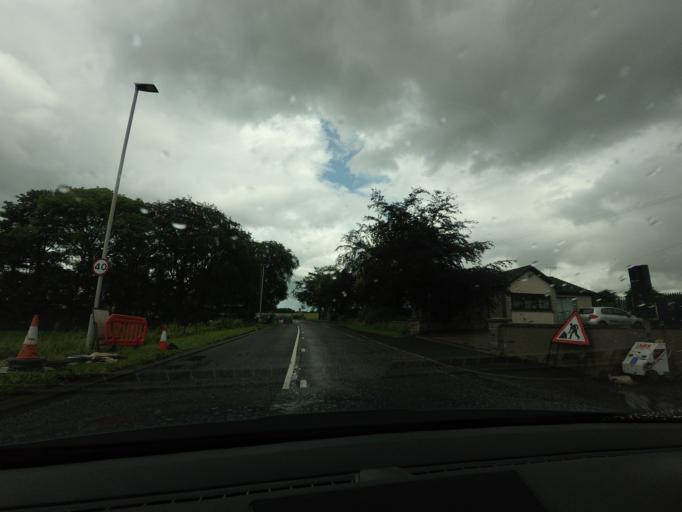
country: GB
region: Scotland
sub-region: Aberdeenshire
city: Turriff
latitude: 57.5446
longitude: -2.4460
